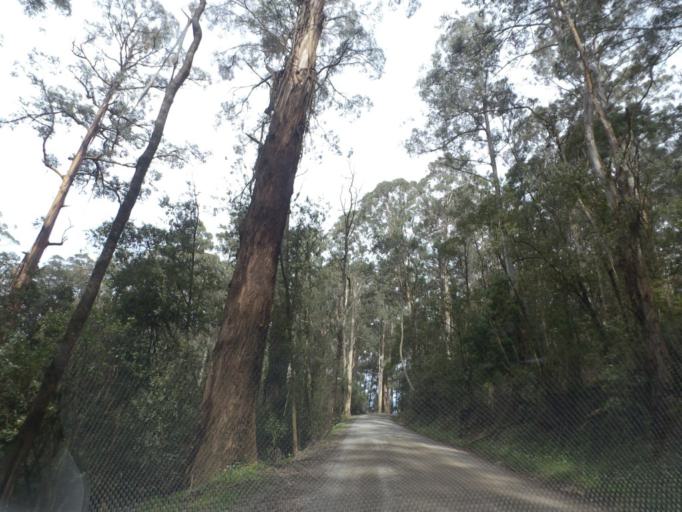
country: AU
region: Victoria
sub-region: Yarra Ranges
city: Mount Dandenong
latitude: -37.8362
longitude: 145.3685
